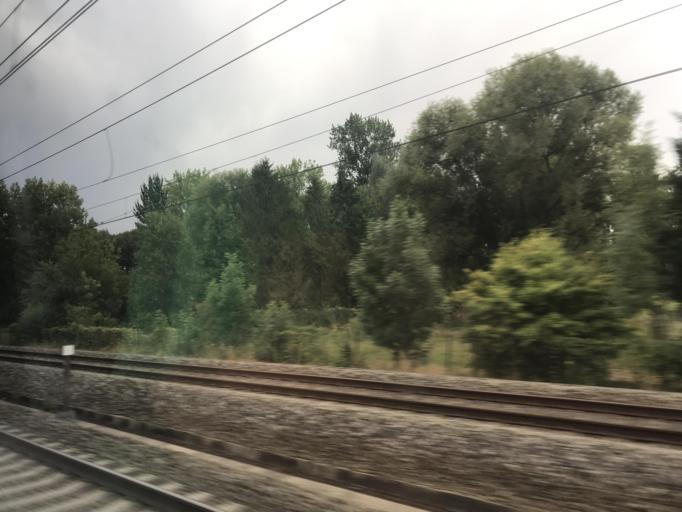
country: BE
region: Flanders
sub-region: Provincie Vlaams-Brabant
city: Bertem
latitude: 50.8977
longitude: 4.5988
